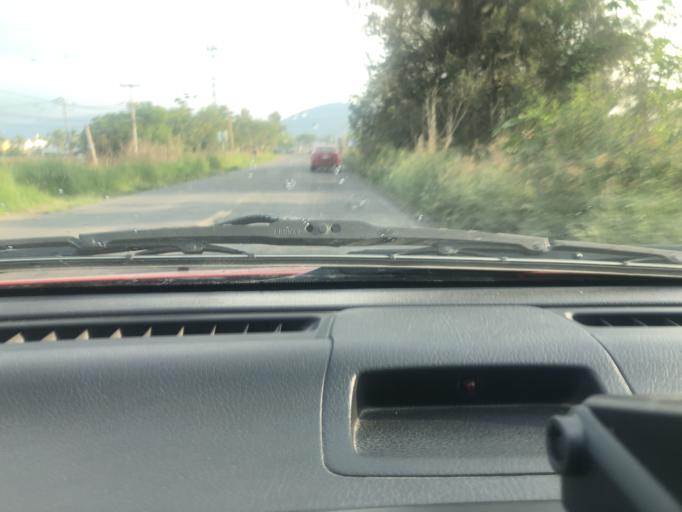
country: MX
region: Jalisco
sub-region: San Pedro Tlaquepaque
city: Santa Anita
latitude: 20.5559
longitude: -103.4180
